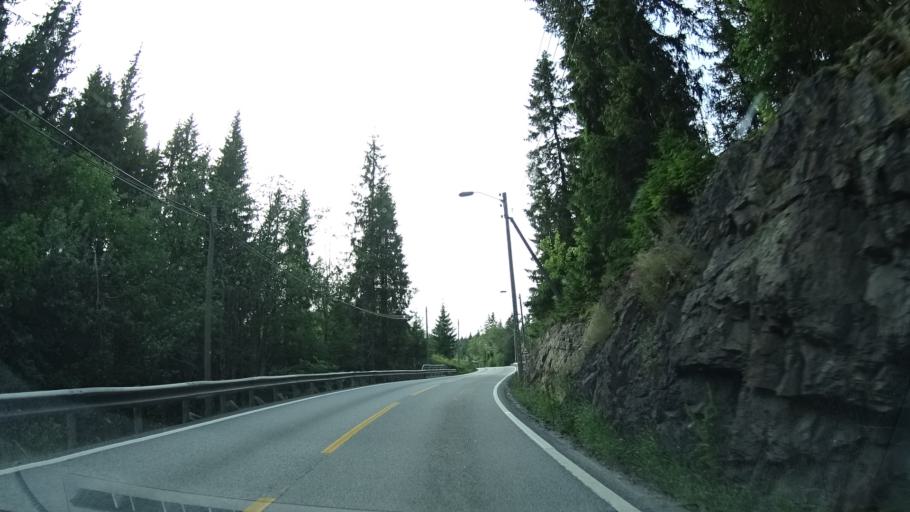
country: NO
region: Akershus
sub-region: Baerum
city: Skui
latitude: 59.9558
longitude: 10.3724
